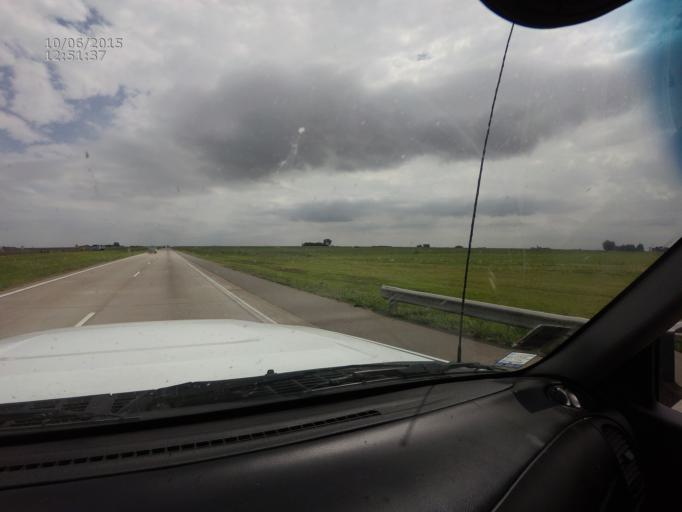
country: AR
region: Santa Fe
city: Armstrong
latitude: -32.8250
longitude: -61.5160
